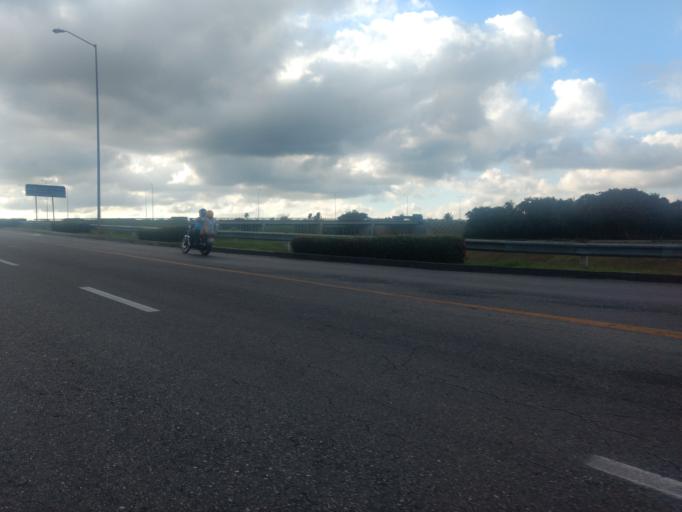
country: CU
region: La Habana
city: Boyeros
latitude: 22.9995
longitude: -82.4109
